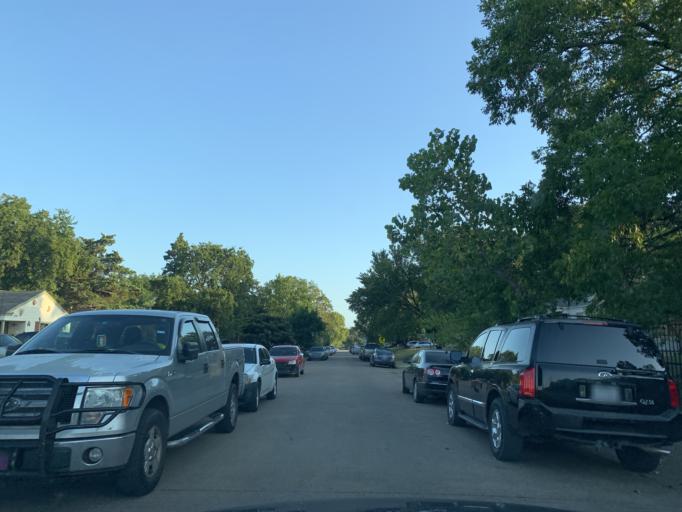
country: US
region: Texas
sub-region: Dallas County
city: Dallas
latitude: 32.7113
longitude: -96.8108
